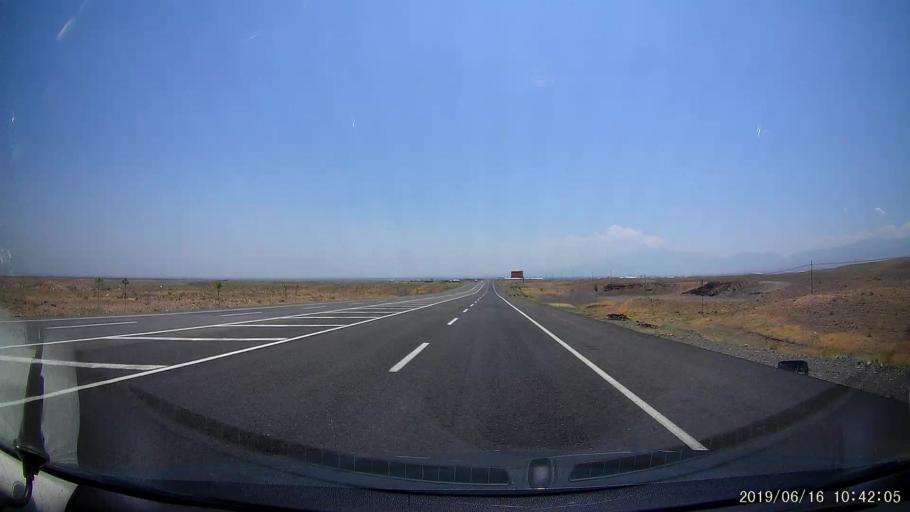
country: AM
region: Armavir
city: Shenavan
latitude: 40.0446
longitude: 43.7988
